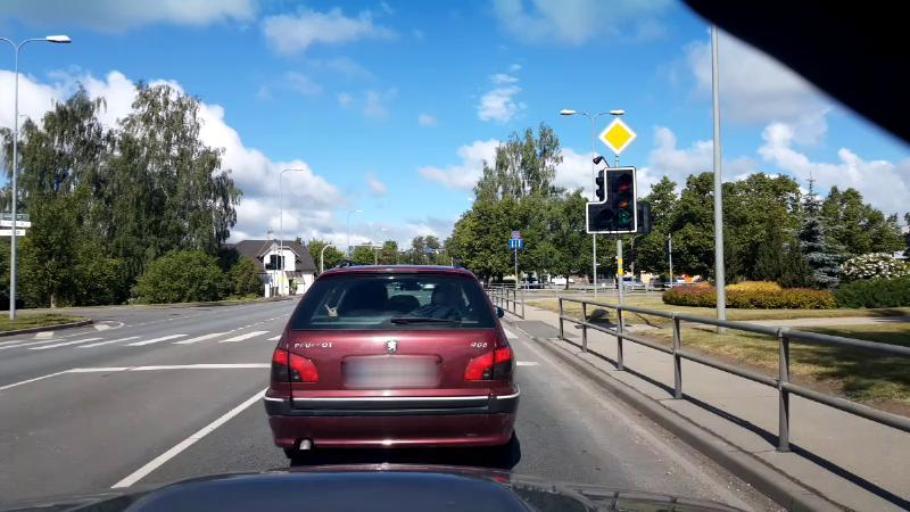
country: LV
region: Bauskas Rajons
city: Bauska
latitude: 56.4067
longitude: 24.1949
